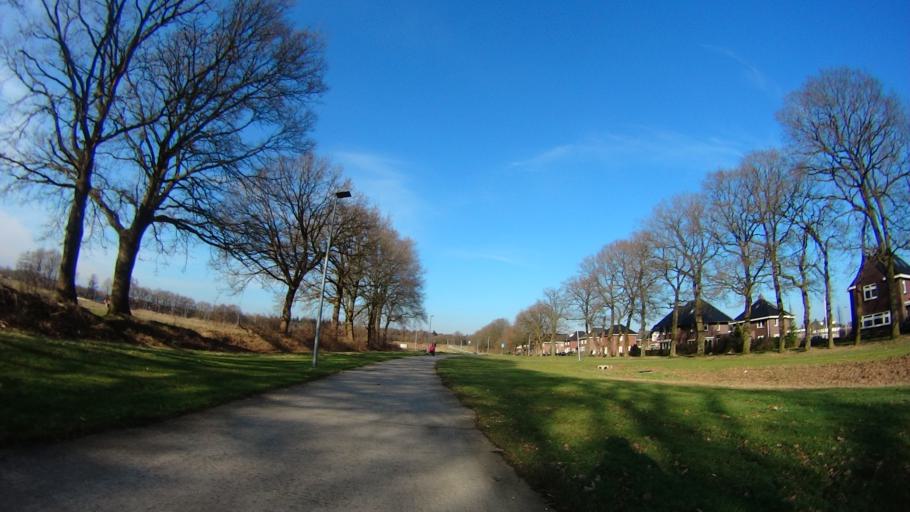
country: NL
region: Drenthe
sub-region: Gemeente Emmen
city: Emmen
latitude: 52.7561
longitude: 6.8638
